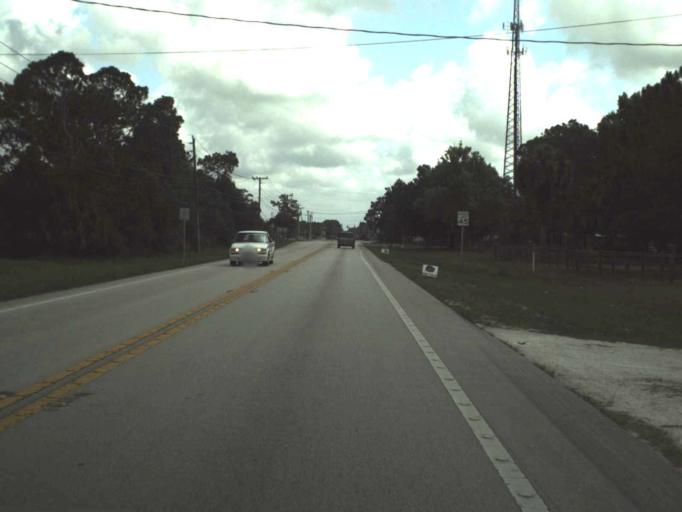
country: US
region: Florida
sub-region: Volusia County
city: Samsula-Spruce Creek
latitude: 29.0072
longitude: -81.0695
